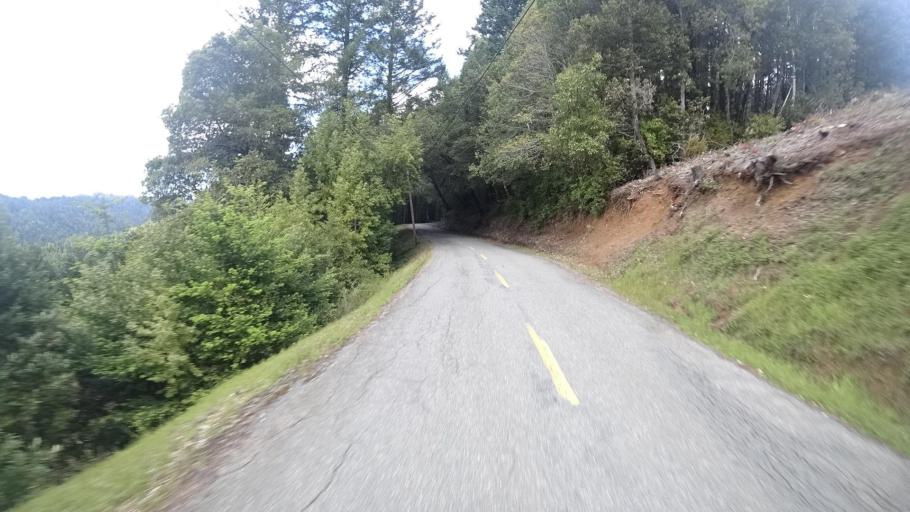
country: US
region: California
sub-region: Humboldt County
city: Blue Lake
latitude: 40.7575
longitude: -123.9702
